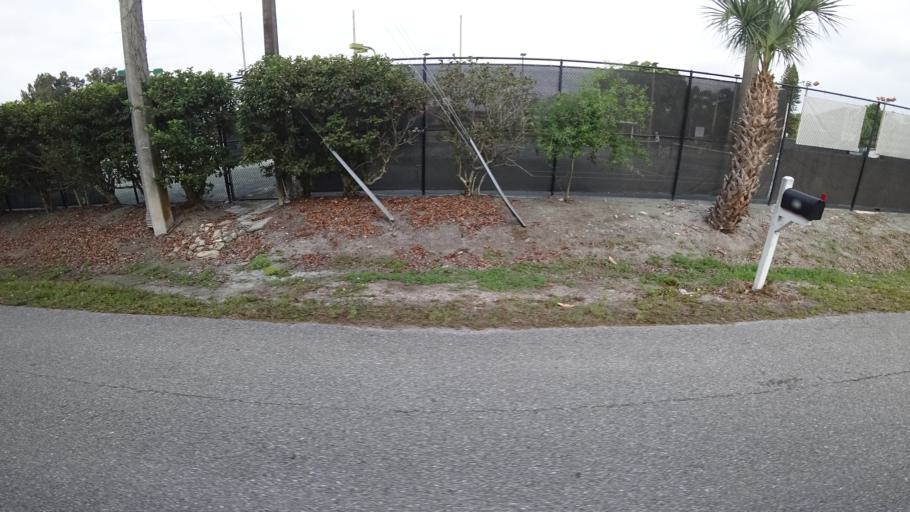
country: US
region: Florida
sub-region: Manatee County
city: West Bradenton
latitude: 27.4914
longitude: -82.6060
